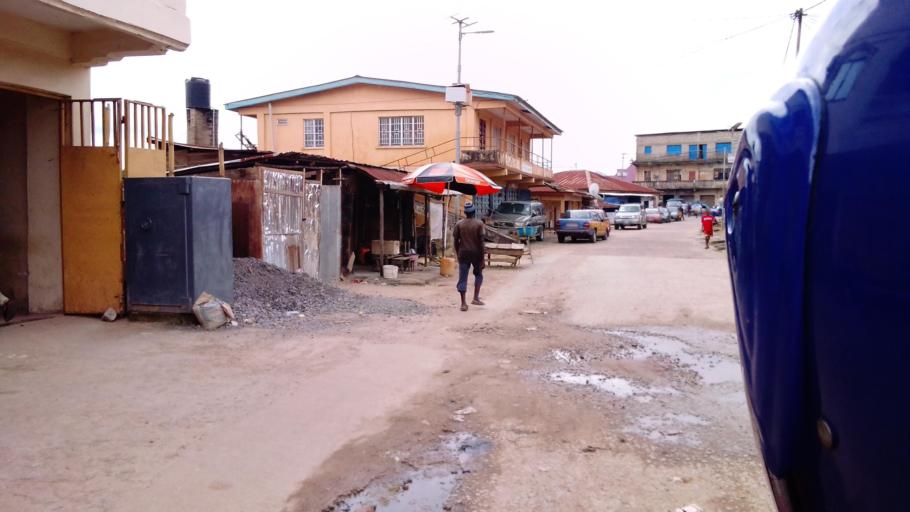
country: SL
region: Eastern Province
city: Koidu
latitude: 8.6441
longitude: -10.9748
